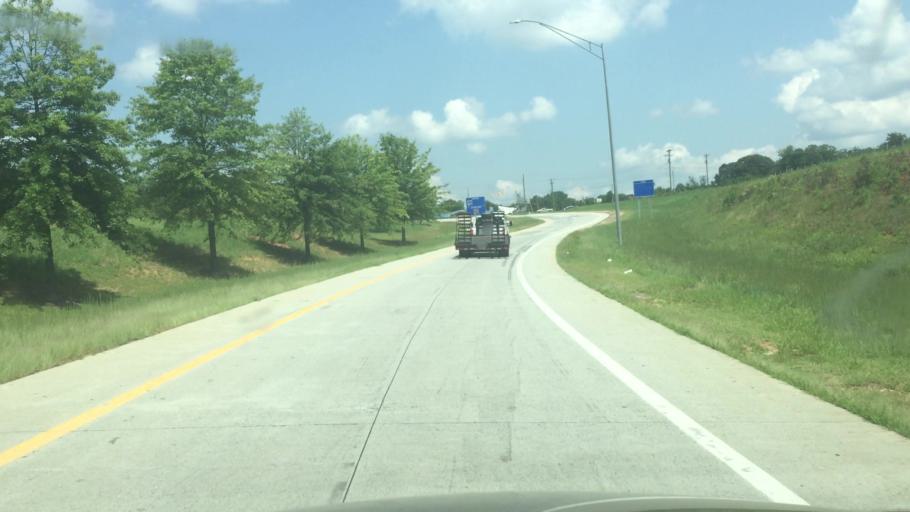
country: US
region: North Carolina
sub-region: Rowan County
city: Salisbury
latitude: 35.6325
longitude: -80.4914
